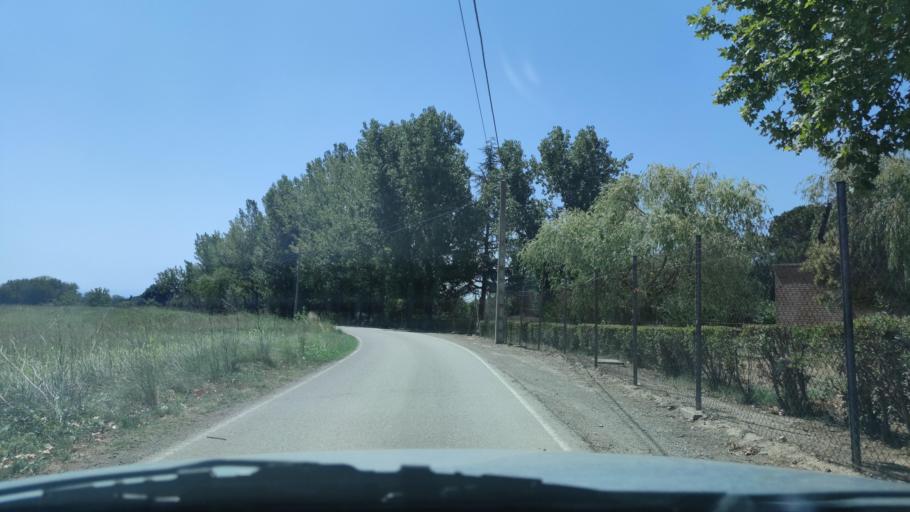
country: ES
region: Catalonia
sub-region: Provincia de Lleida
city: Alpicat
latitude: 41.6460
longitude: 0.5733
